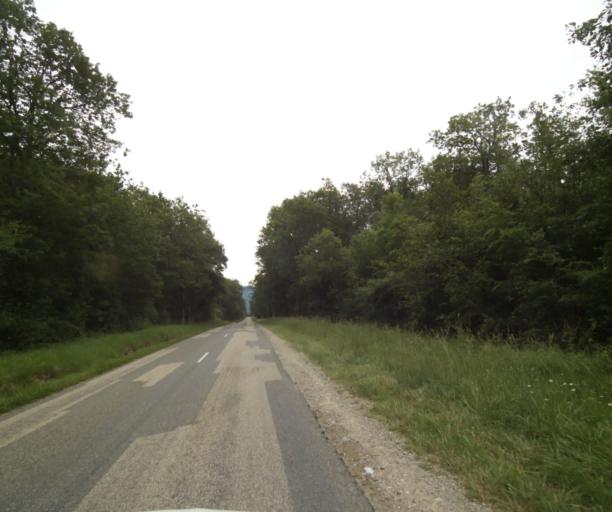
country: FR
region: Rhone-Alpes
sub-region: Departement de la Haute-Savoie
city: Sciez
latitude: 46.3133
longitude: 6.4024
